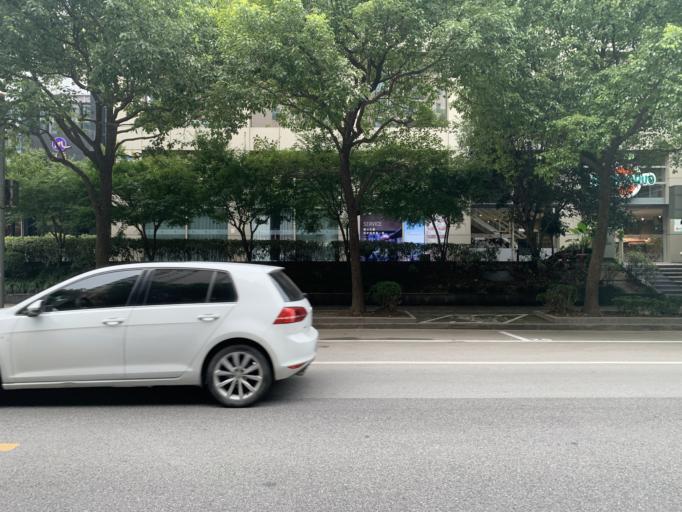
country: CN
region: Shanghai Shi
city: Huamu
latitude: 31.2283
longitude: 121.5567
